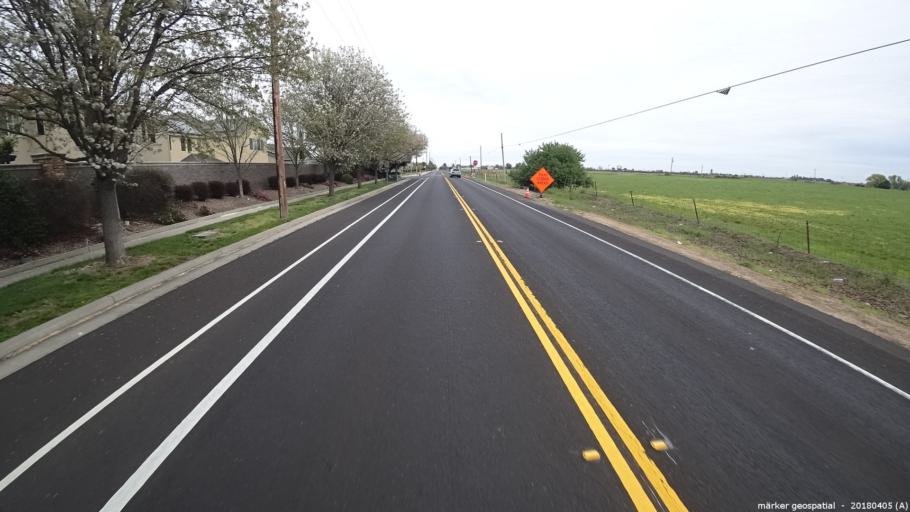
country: US
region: California
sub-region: Sacramento County
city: Laguna
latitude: 38.3794
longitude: -121.4323
